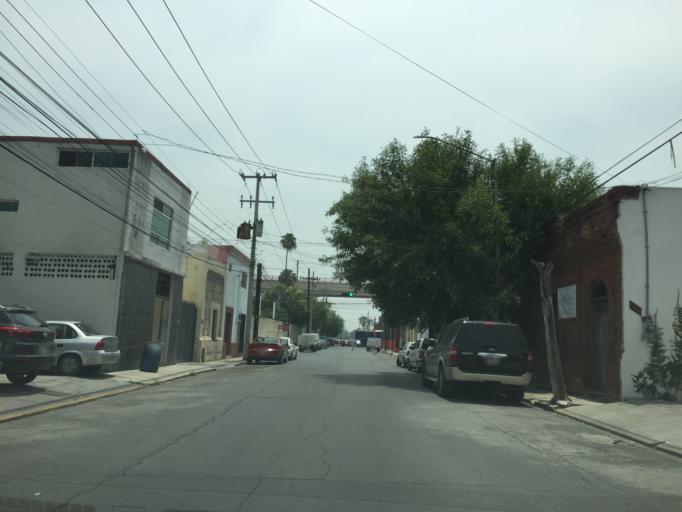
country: MX
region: Nuevo Leon
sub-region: Monterrey
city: Monterrey
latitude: 25.6798
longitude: -100.2989
